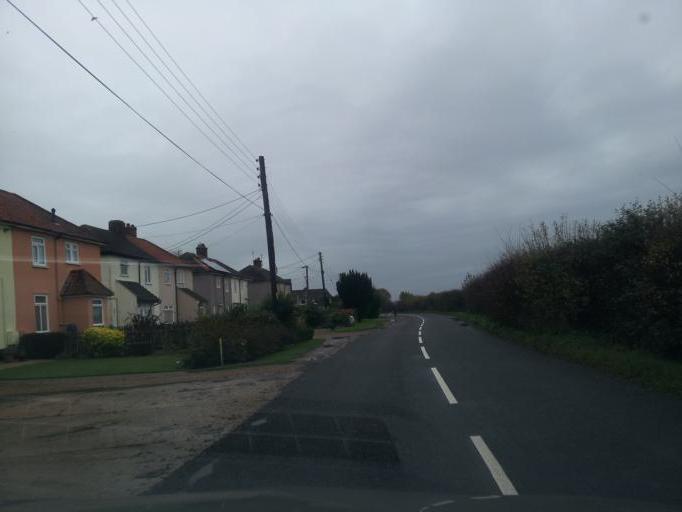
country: GB
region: England
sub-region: Essex
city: Eight Ash Green
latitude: 51.9216
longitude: 0.8012
